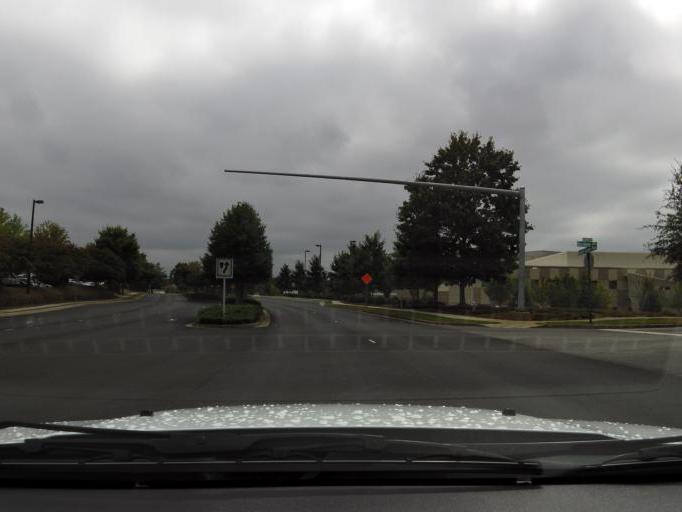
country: US
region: Georgia
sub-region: Cobb County
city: Kennesaw
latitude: 34.0387
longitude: -84.5736
